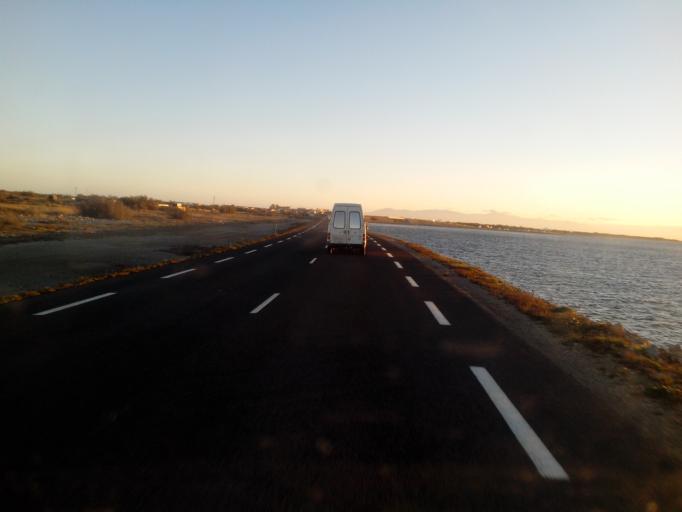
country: FR
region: Languedoc-Roussillon
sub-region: Departement de l'Aude
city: Leucate
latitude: 42.8940
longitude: 3.0480
